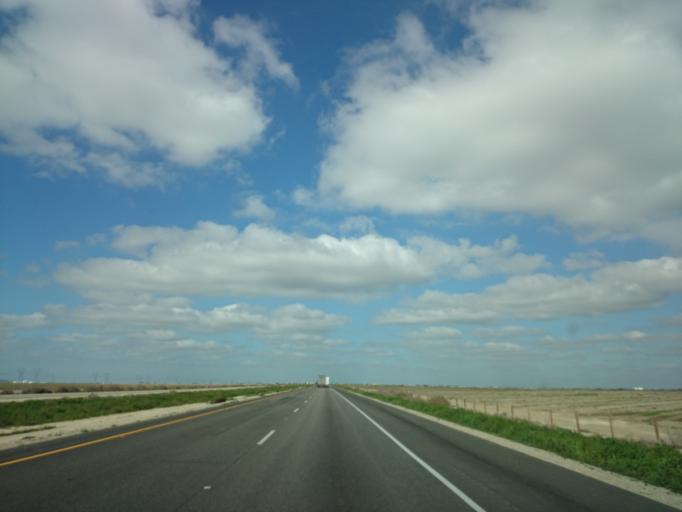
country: US
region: California
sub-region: Kern County
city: Rosedale
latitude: 35.2459
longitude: -119.2017
